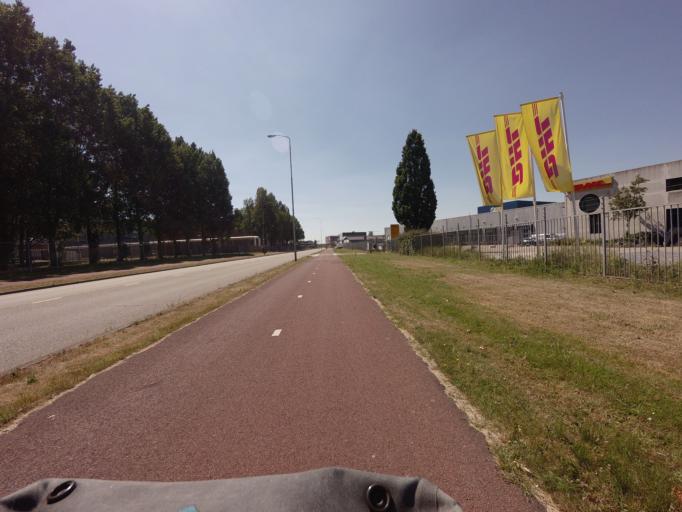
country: NL
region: Utrecht
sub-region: Stichtse Vecht
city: Maarssen
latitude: 52.1039
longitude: 5.0680
